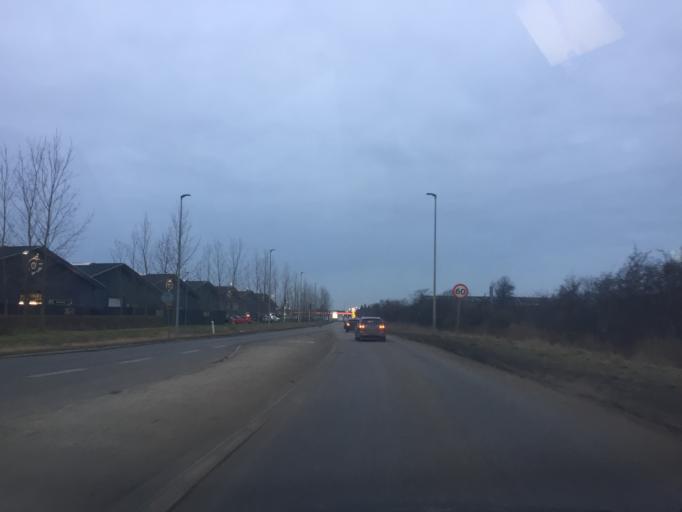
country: DK
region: Zealand
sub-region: Koge Kommune
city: Koge
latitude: 55.4796
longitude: 12.1919
